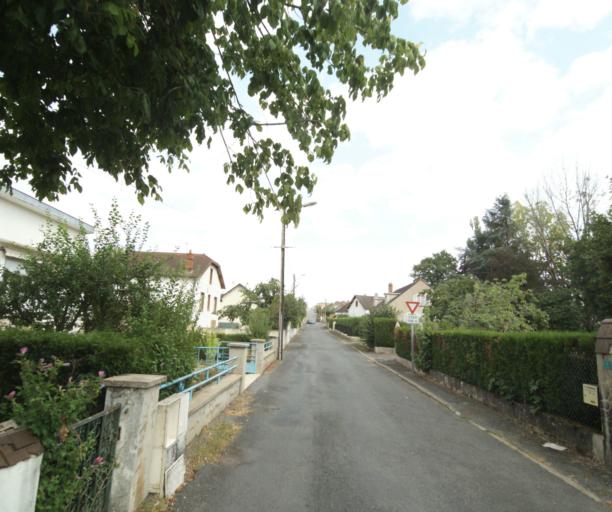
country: FR
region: Bourgogne
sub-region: Departement de Saone-et-Loire
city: Gueugnon
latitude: 46.6059
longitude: 4.0736
